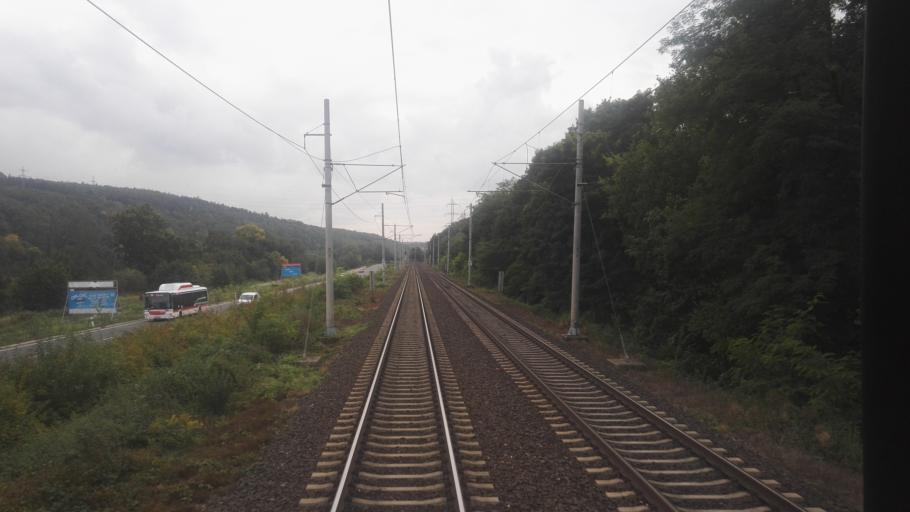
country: CZ
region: Central Bohemia
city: Roztoky
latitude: 50.1476
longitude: 14.3970
